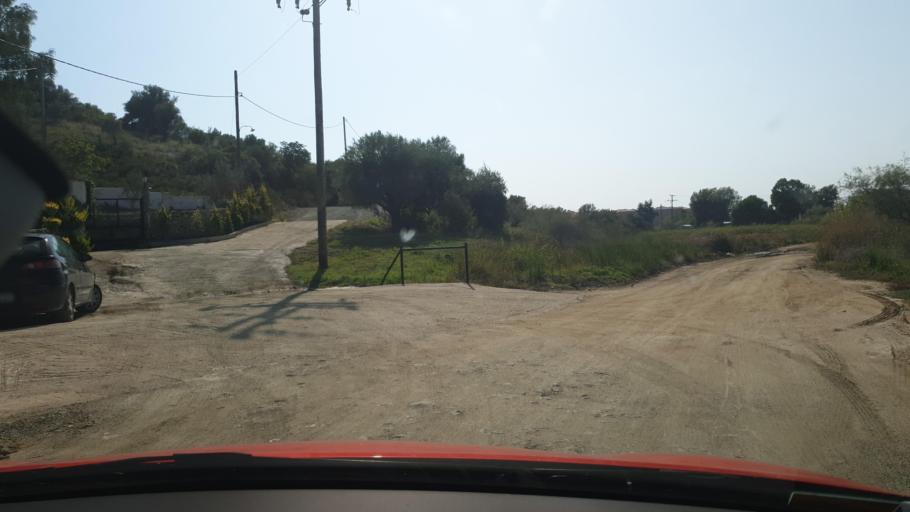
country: GR
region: Central Macedonia
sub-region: Nomos Chalkidikis
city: Sykia
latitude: 39.9793
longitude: 23.9082
